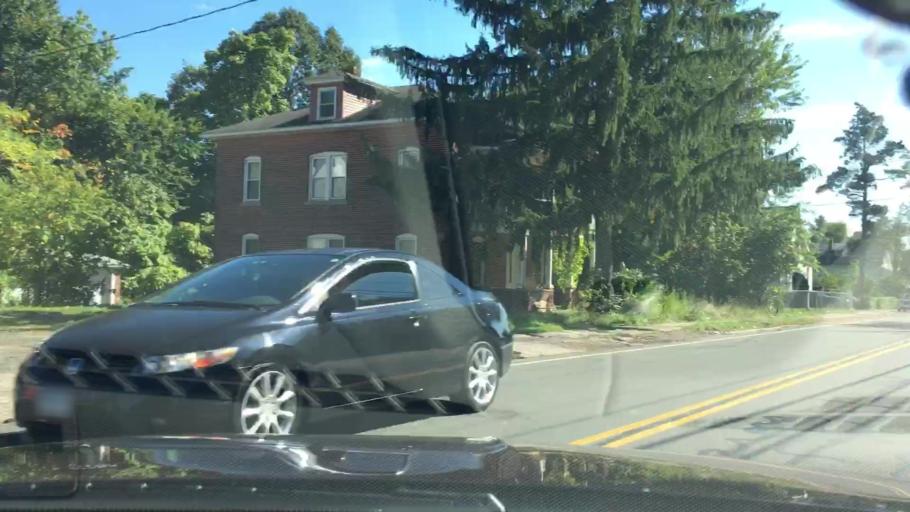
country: US
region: Connecticut
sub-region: Hartford County
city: New Britain
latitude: 41.6585
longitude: -72.7644
